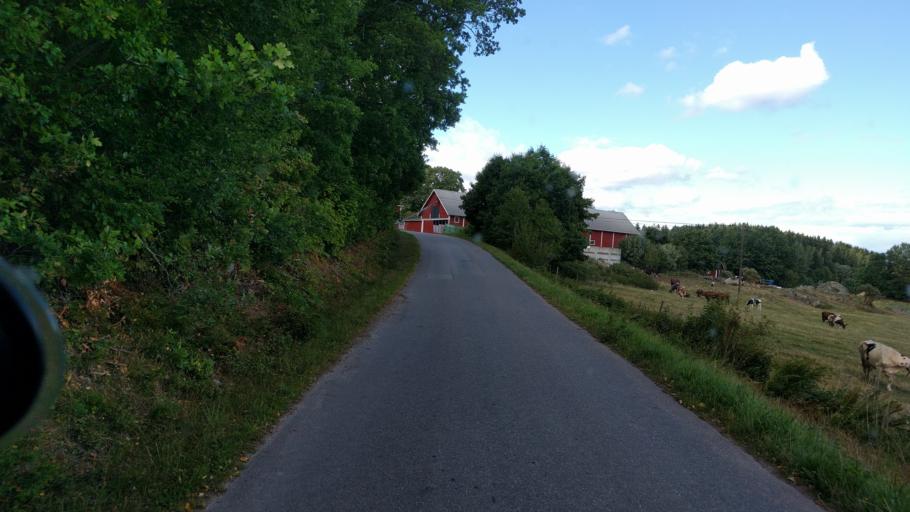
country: SE
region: Kalmar
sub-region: Vasterviks Kommun
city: Ankarsrum
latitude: 57.8010
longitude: 16.1724
